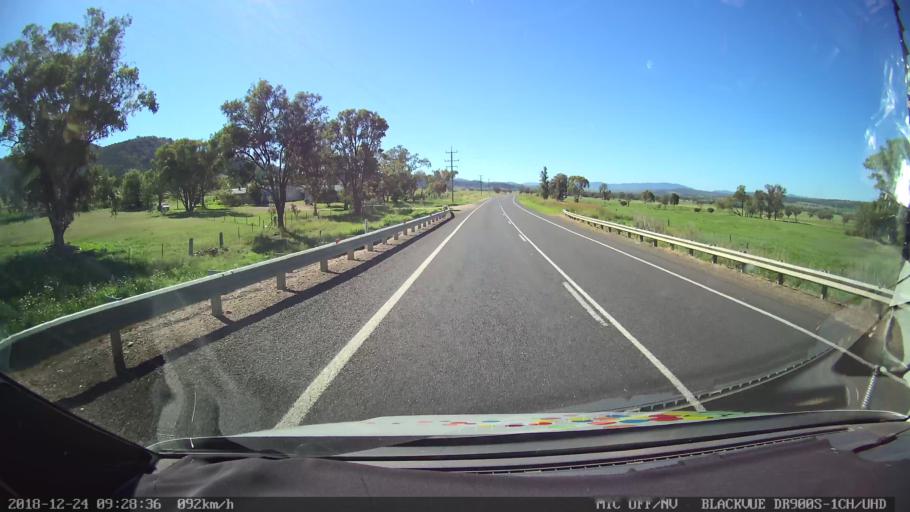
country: AU
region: New South Wales
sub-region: Liverpool Plains
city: Quirindi
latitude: -31.5396
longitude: 150.6901
